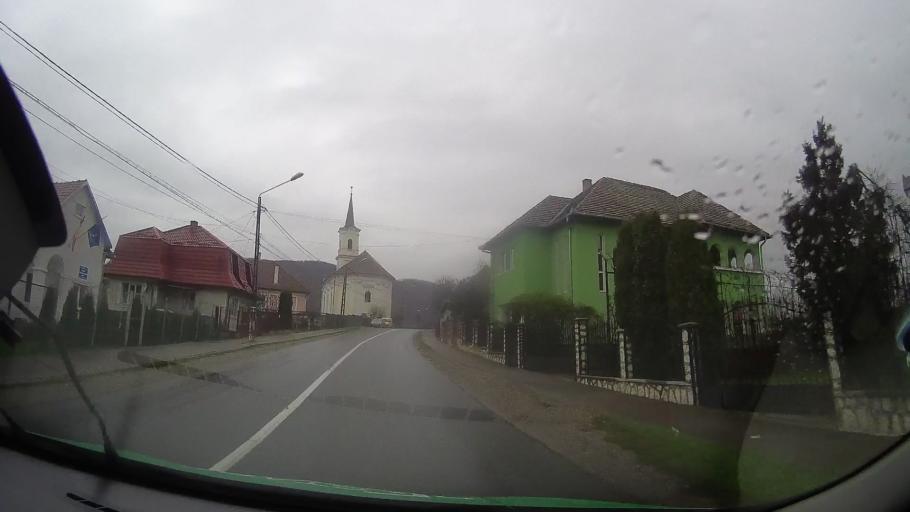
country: RO
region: Bistrita-Nasaud
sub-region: Municipiul Bistrita
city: Viisoara
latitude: 47.0718
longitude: 24.4364
